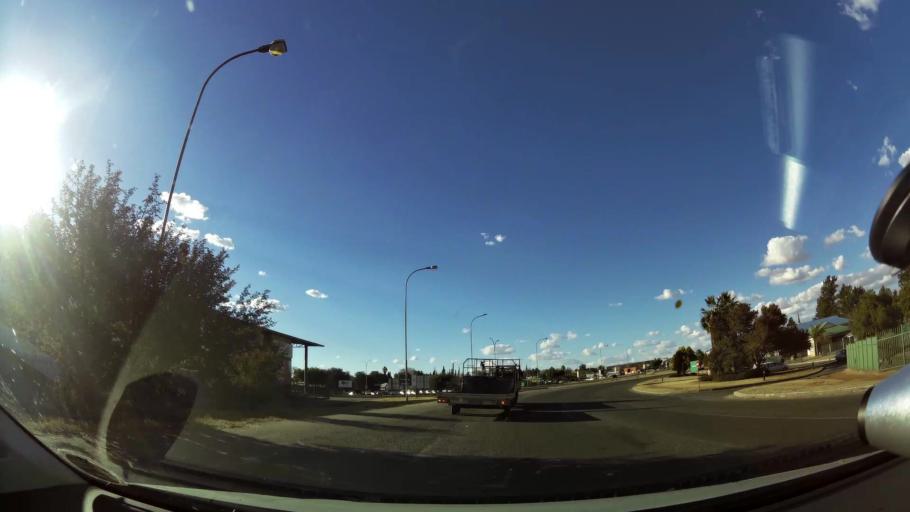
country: ZA
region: North-West
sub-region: Dr Kenneth Kaunda District Municipality
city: Klerksdorp
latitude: -26.8606
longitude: 26.6693
